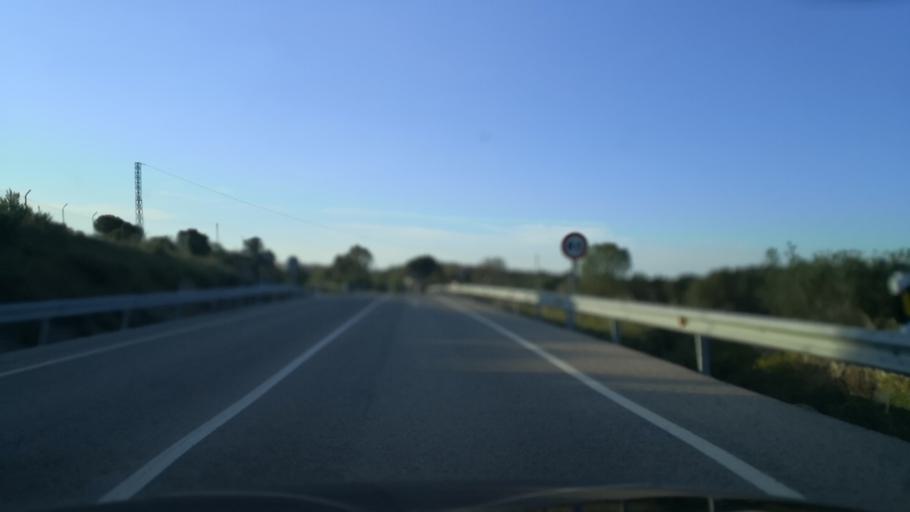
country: ES
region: Extremadura
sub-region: Provincia de Caceres
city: Valencia de Alcantara
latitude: 39.3922
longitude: -7.2462
